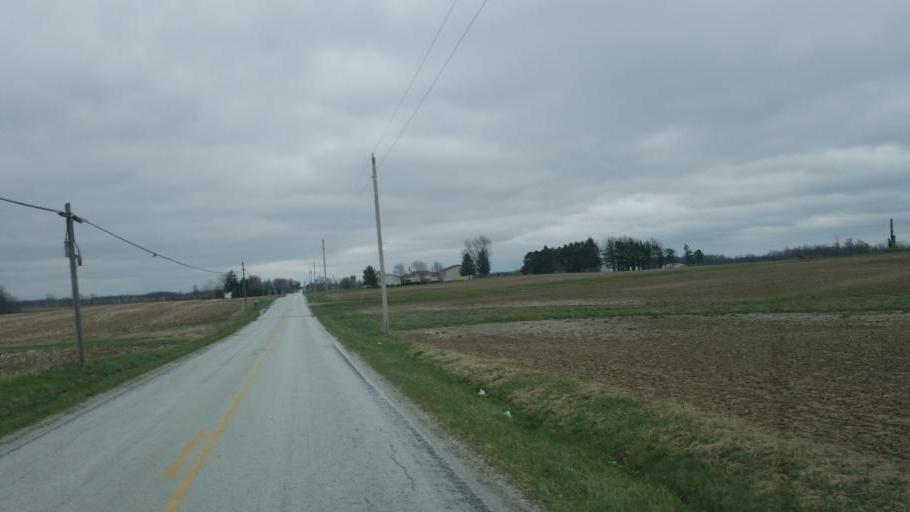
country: US
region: Ohio
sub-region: Hardin County
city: Kenton
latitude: 40.6588
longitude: -83.5660
